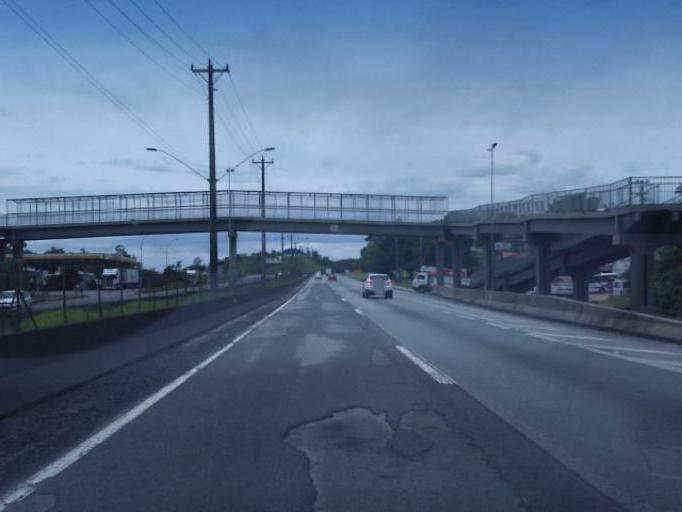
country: BR
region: Sao Paulo
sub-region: Sao Lourenco Da Serra
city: Sao Lourenco da Serra
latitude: -23.8950
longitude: -46.9854
